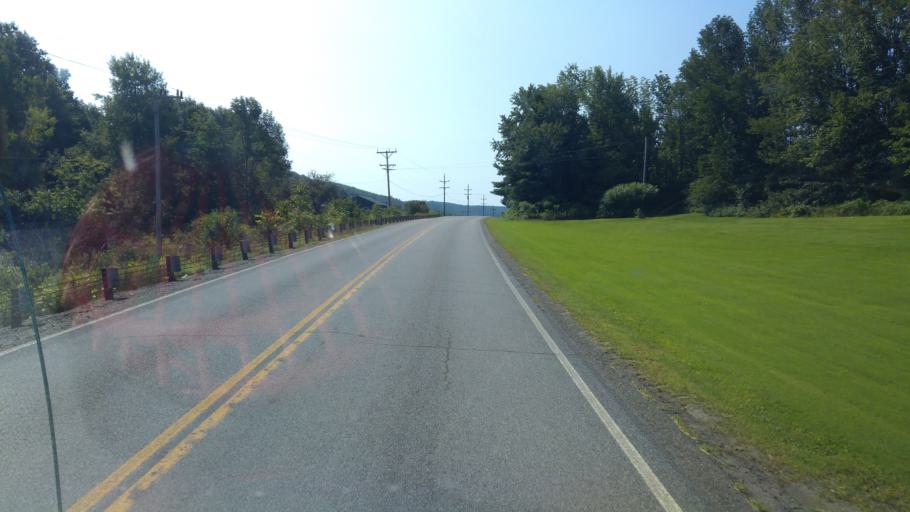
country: US
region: New York
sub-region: Allegany County
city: Friendship
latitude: 42.1607
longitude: -78.1484
